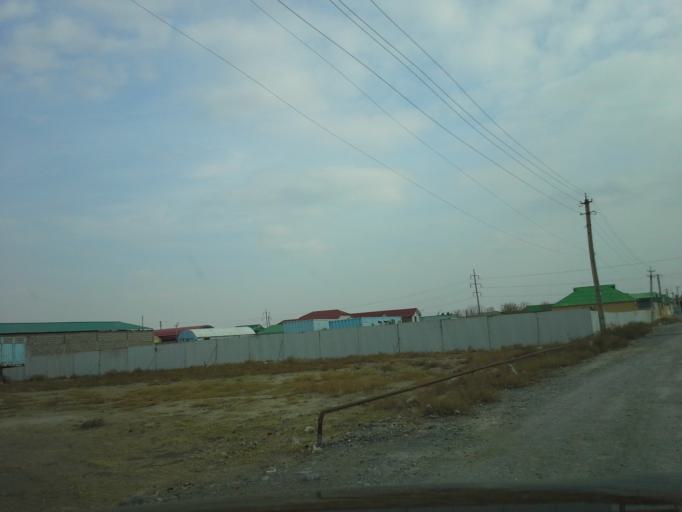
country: TM
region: Ahal
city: Abadan
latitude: 38.0378
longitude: 58.2513
